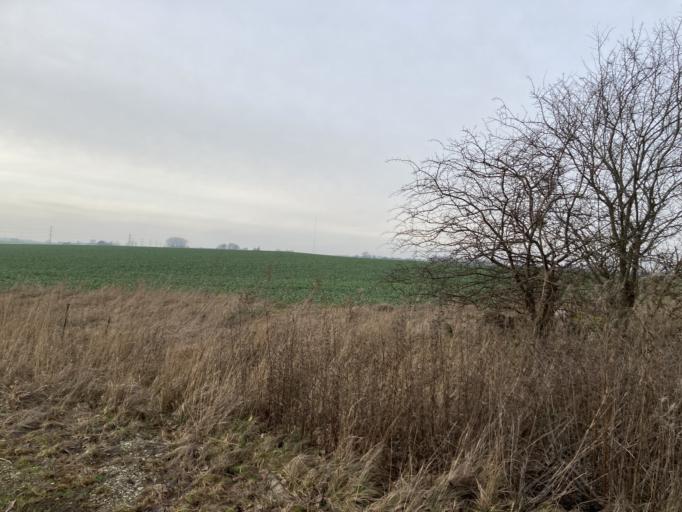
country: DK
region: Capital Region
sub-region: Hoje-Taastrup Kommune
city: Taastrup
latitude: 55.6919
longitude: 12.2798
